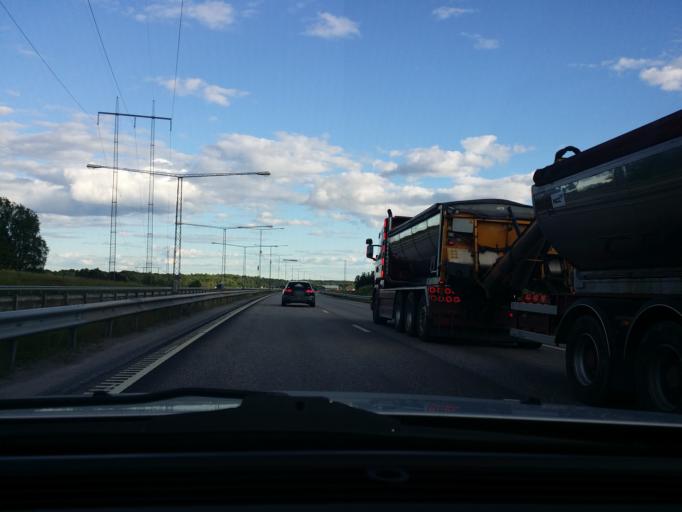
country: SE
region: Stockholm
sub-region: Sigtuna Kommun
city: Rosersberg
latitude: 59.5827
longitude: 17.9005
